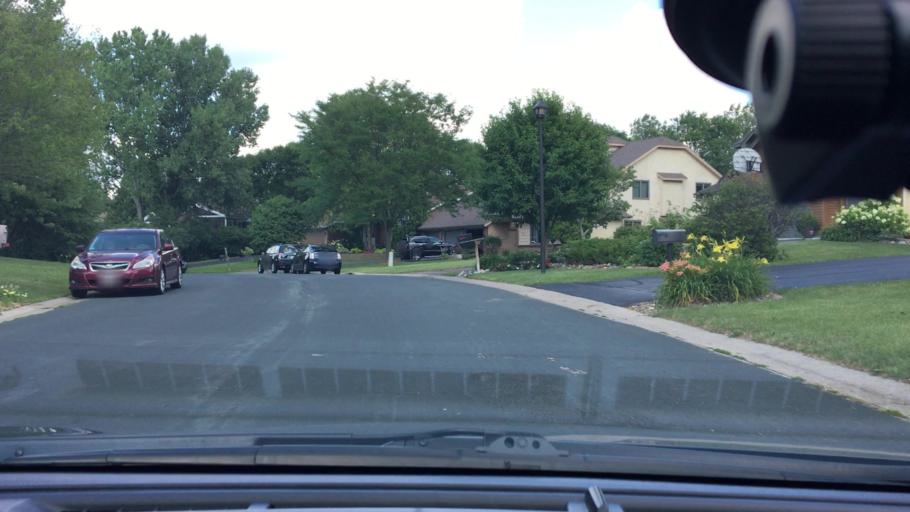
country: US
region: Minnesota
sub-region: Hennepin County
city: Plymouth
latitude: 45.0391
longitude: -93.4303
